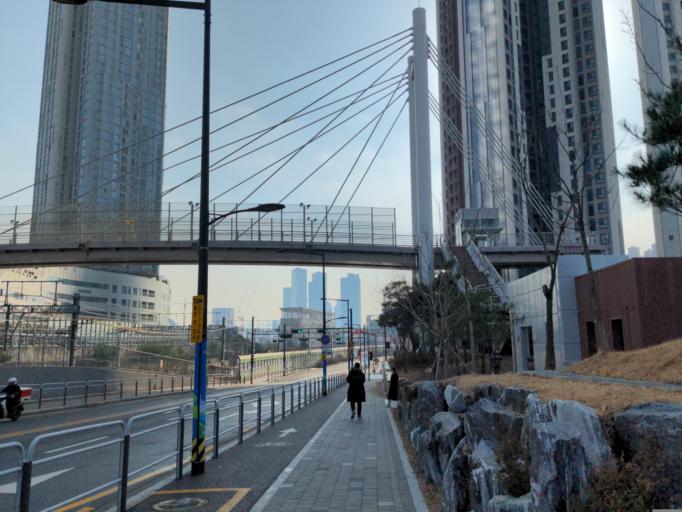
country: KR
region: Seoul
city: Seoul
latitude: 37.5573
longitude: 127.0391
